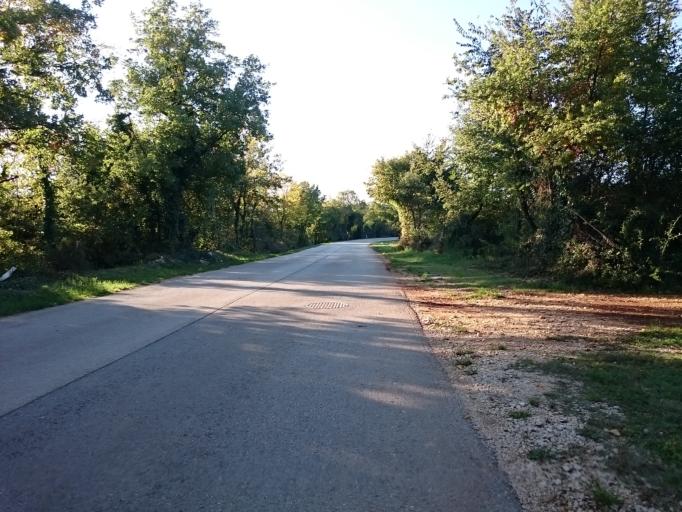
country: HR
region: Istarska
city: Novigrad
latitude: 45.2951
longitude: 13.6336
